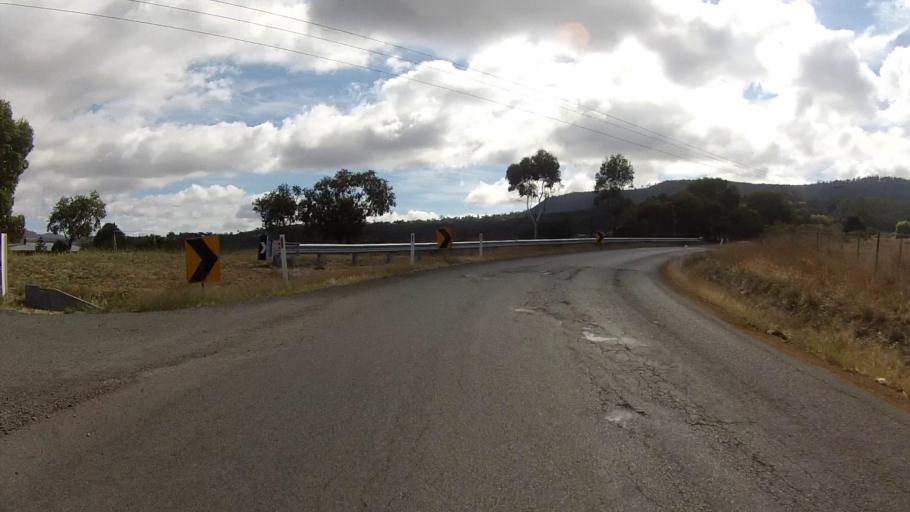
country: AU
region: Tasmania
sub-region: Brighton
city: Old Beach
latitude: -42.7597
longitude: 147.3013
